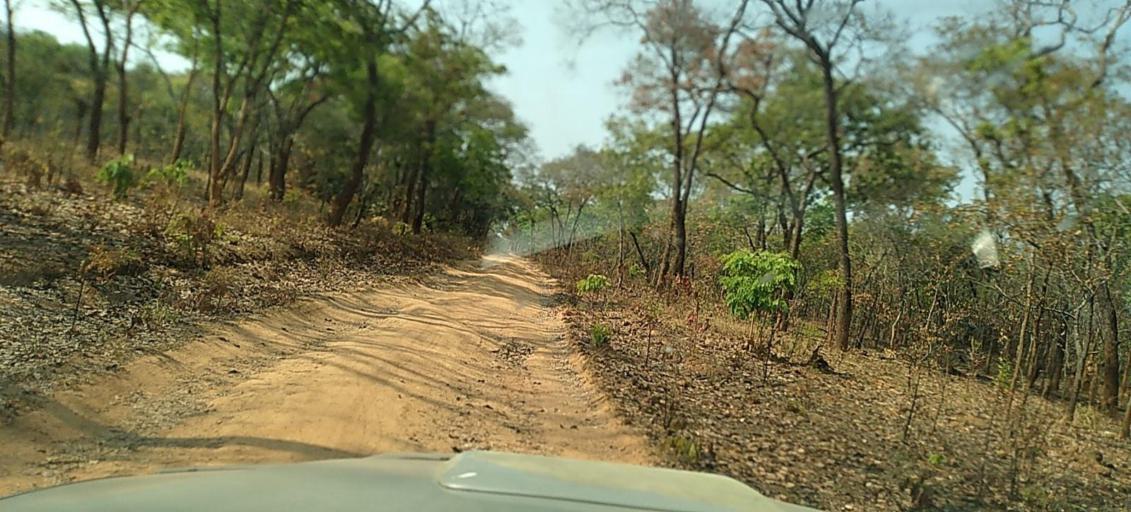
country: ZM
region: North-Western
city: Kasempa
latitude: -13.5315
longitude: 26.4085
